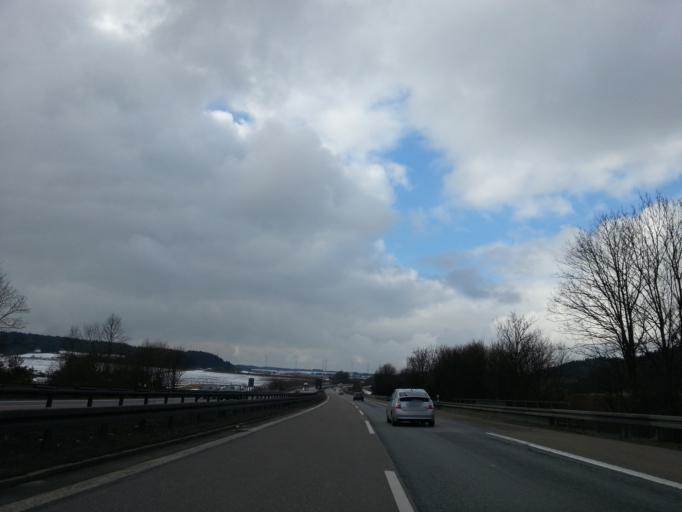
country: DE
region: Bavaria
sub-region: Upper Palatinate
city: Velburg
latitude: 49.2019
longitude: 11.6701
